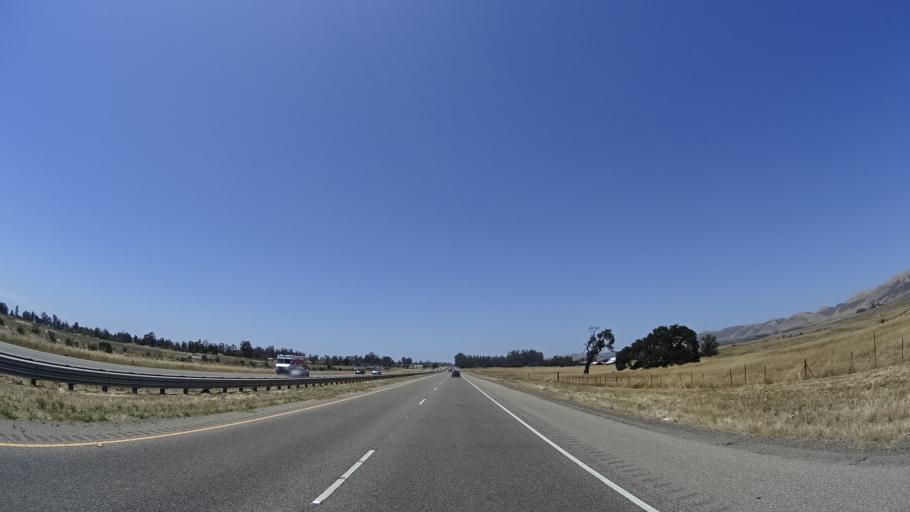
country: US
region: California
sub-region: San Luis Obispo County
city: Nipomo
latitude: 35.0173
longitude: -120.4633
